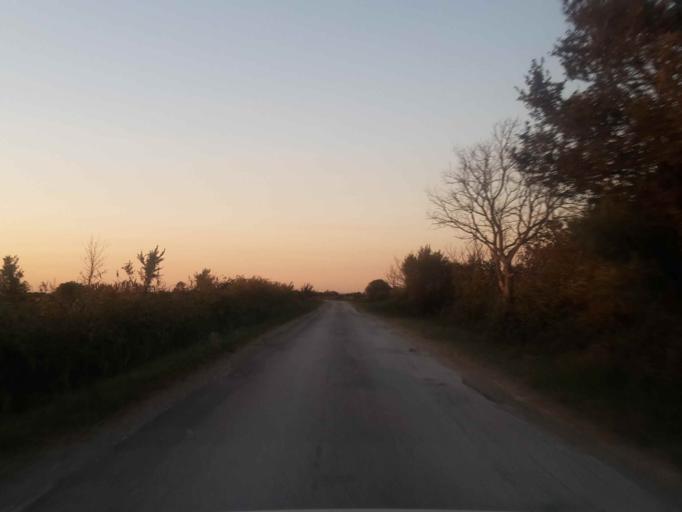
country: FR
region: Provence-Alpes-Cote d'Azur
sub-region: Departement des Bouches-du-Rhone
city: Port-Saint-Louis-du-Rhone
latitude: 43.4140
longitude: 4.6933
